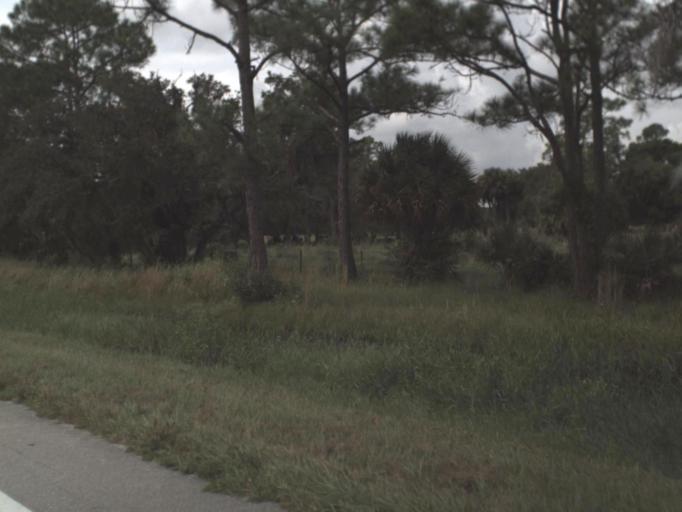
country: US
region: Florida
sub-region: Hendry County
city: Port LaBelle
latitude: 26.8417
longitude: -81.3876
